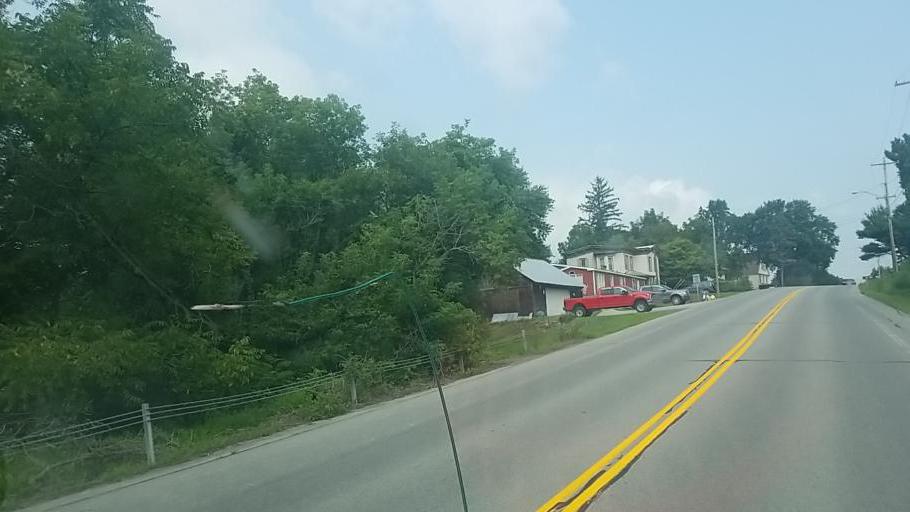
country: US
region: New York
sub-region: Montgomery County
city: Fort Plain
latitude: 42.9375
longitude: -74.6156
